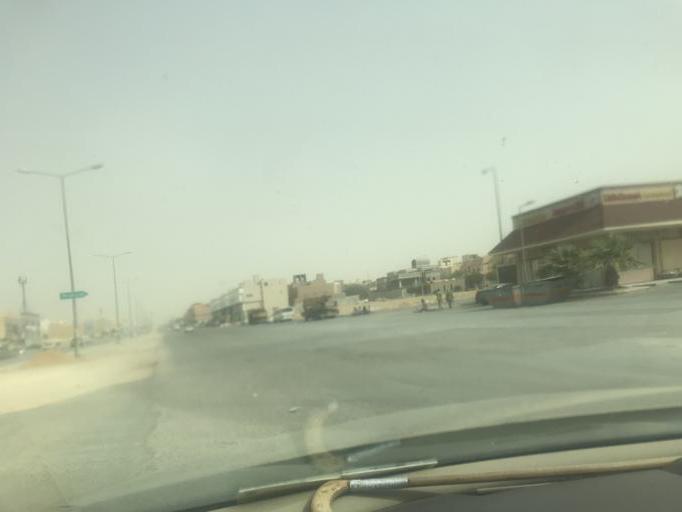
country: SA
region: Ar Riyad
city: Riyadh
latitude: 24.8030
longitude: 46.6043
